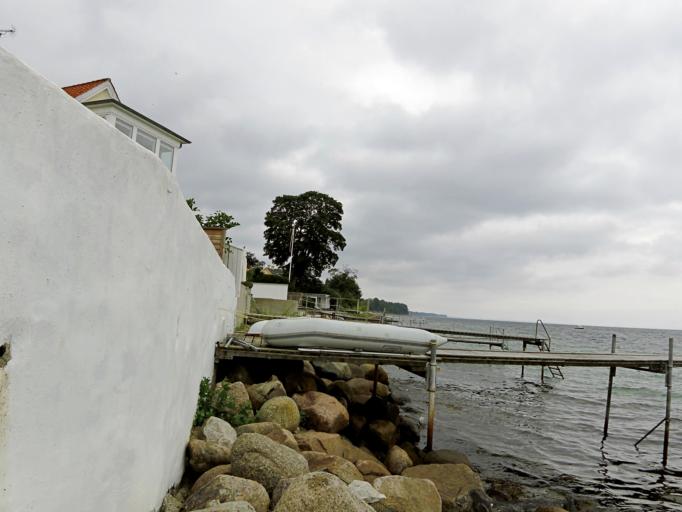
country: DK
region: Capital Region
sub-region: Gentofte Kommune
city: Charlottenlund
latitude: 55.7888
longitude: 12.5951
